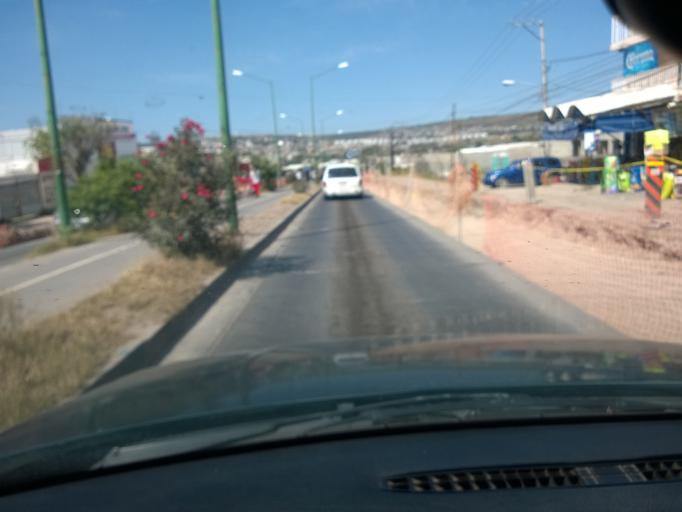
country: MX
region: Guanajuato
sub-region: Leon
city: Ejido la Joya
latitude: 21.1386
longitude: -101.7310
